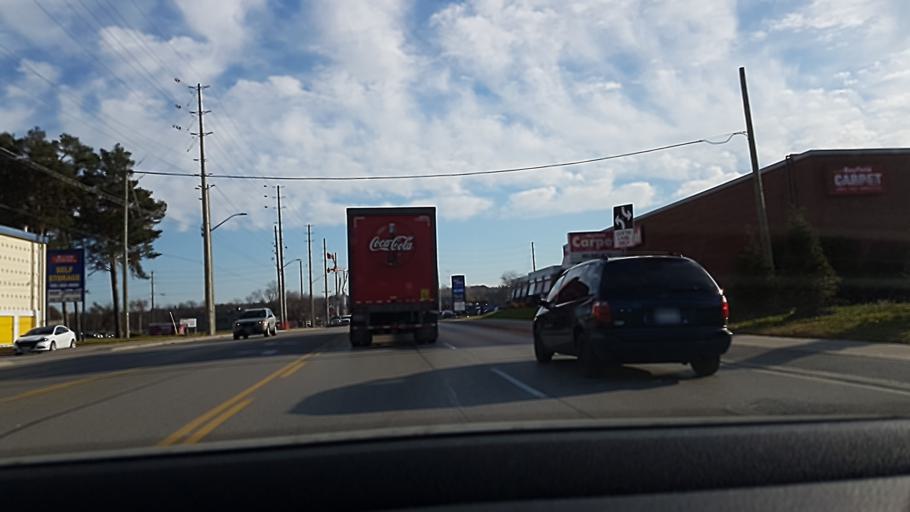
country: CA
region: Ontario
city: Barrie
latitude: 44.3767
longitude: -79.7002
